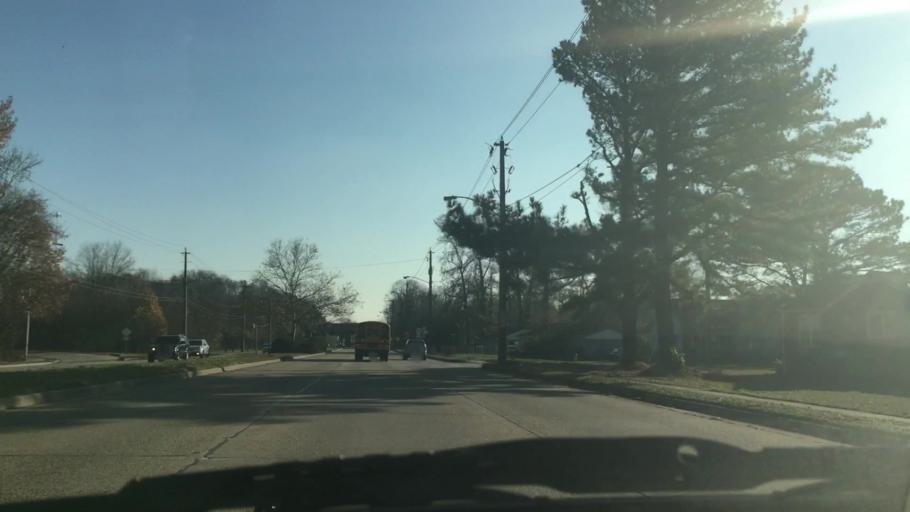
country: US
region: Virginia
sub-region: City of Norfolk
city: Norfolk
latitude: 36.9061
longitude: -76.2402
